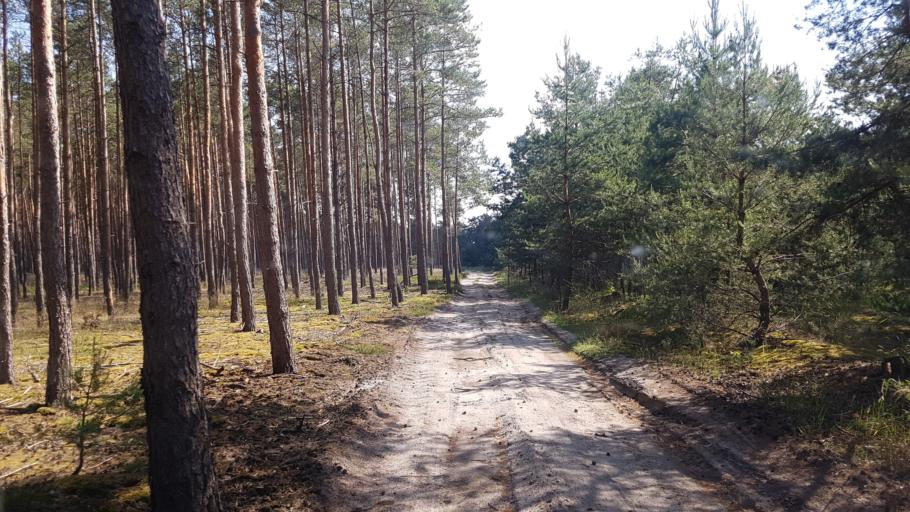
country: DE
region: Brandenburg
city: Trobitz
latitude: 51.6473
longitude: 13.4346
